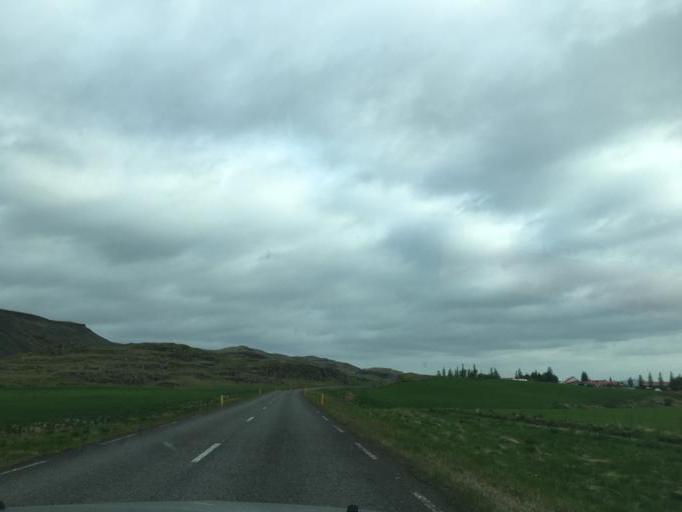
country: IS
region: South
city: Vestmannaeyjar
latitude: 64.1920
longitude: -20.2778
